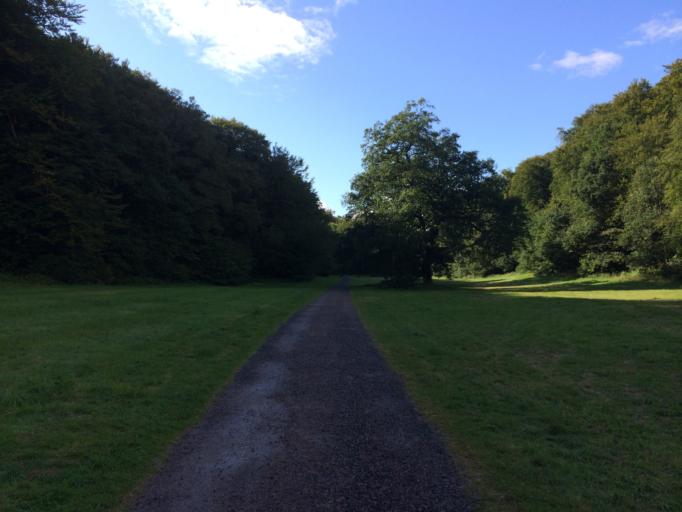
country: SE
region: Skane
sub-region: Klippans Kommun
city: Ljungbyhed
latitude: 56.0041
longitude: 13.2819
